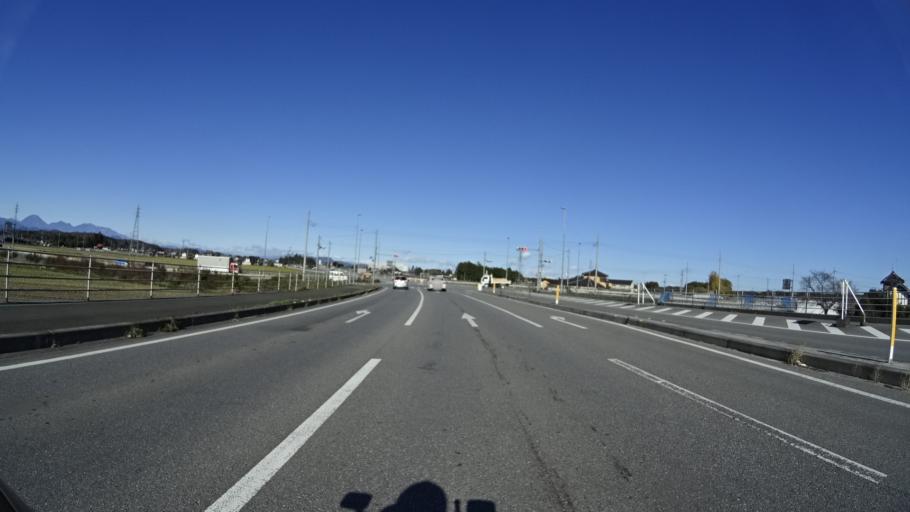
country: JP
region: Tochigi
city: Mibu
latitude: 36.4769
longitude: 139.7541
